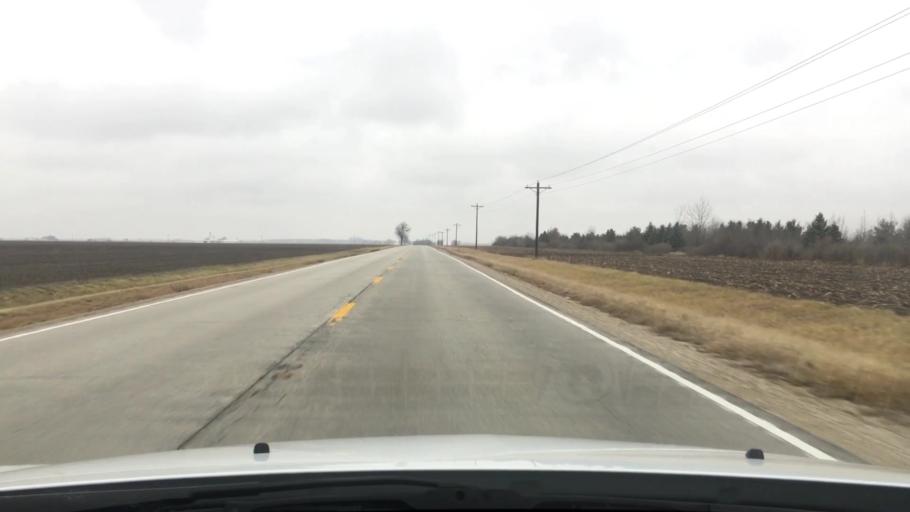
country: US
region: Illinois
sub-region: Iroquois County
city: Clifton
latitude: 40.8871
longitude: -87.8738
